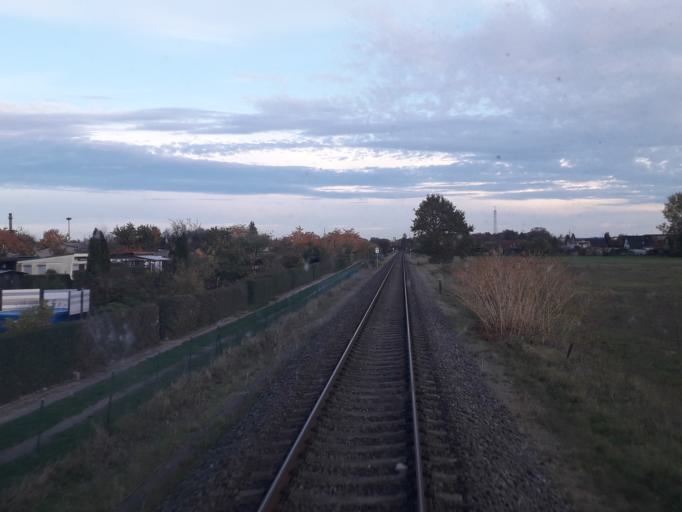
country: DE
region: Brandenburg
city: Neuruppin
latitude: 52.9265
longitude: 12.7771
